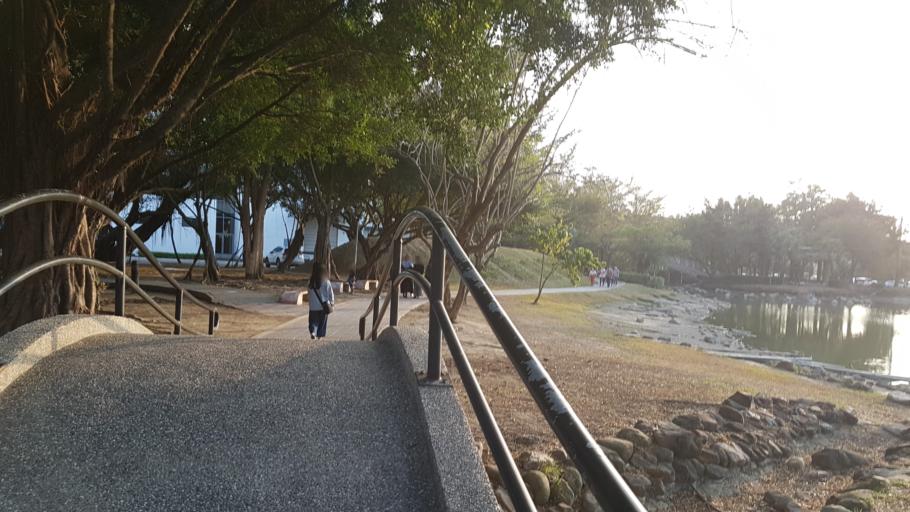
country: TW
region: Taiwan
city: Xinying
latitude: 23.3093
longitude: 120.3151
